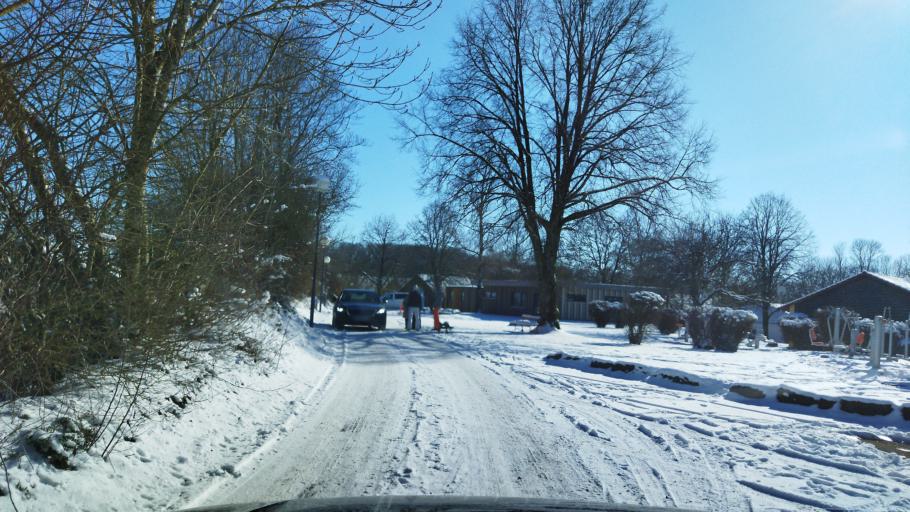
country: DE
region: Baden-Wuerttemberg
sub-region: Regierungsbezirk Stuttgart
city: Langenburg
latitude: 49.2480
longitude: 9.8641
